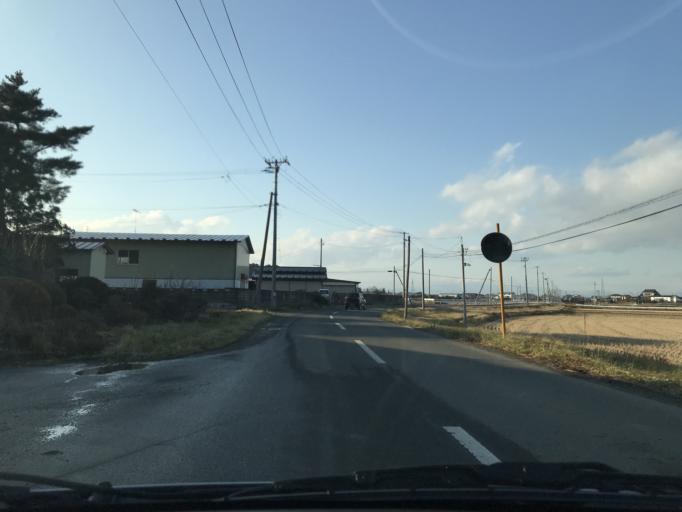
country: JP
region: Miyagi
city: Wakuya
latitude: 38.7160
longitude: 141.1454
